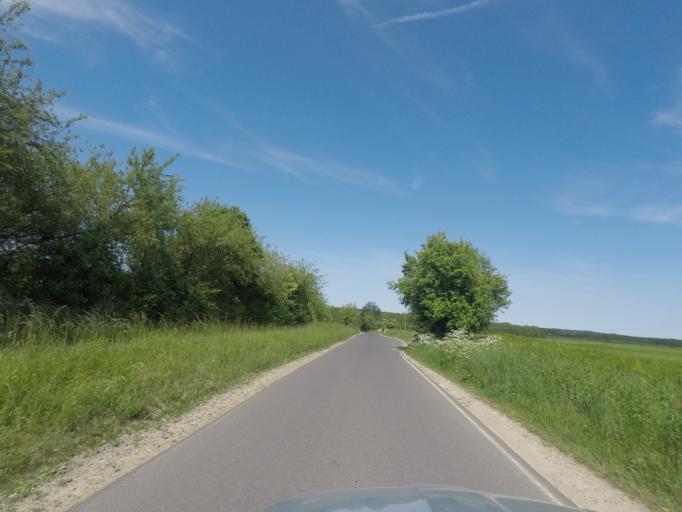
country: DE
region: Brandenburg
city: Britz
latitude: 52.8842
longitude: 13.7678
